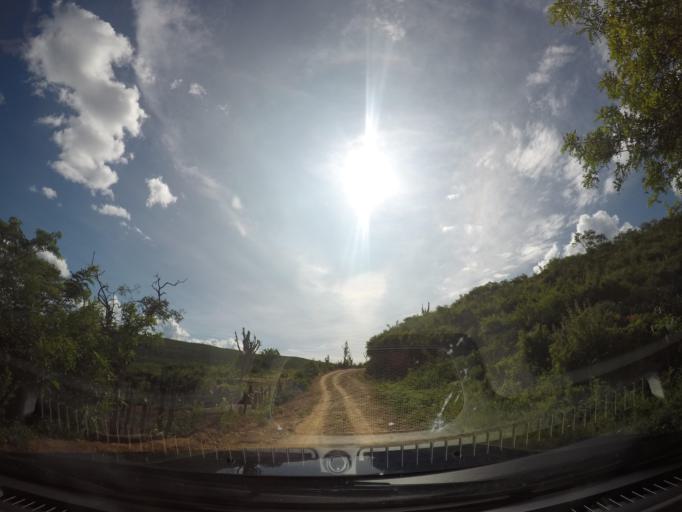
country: BR
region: Bahia
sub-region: Barra Da Estiva
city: Barra da Estiva
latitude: -13.1964
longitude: -41.5895
